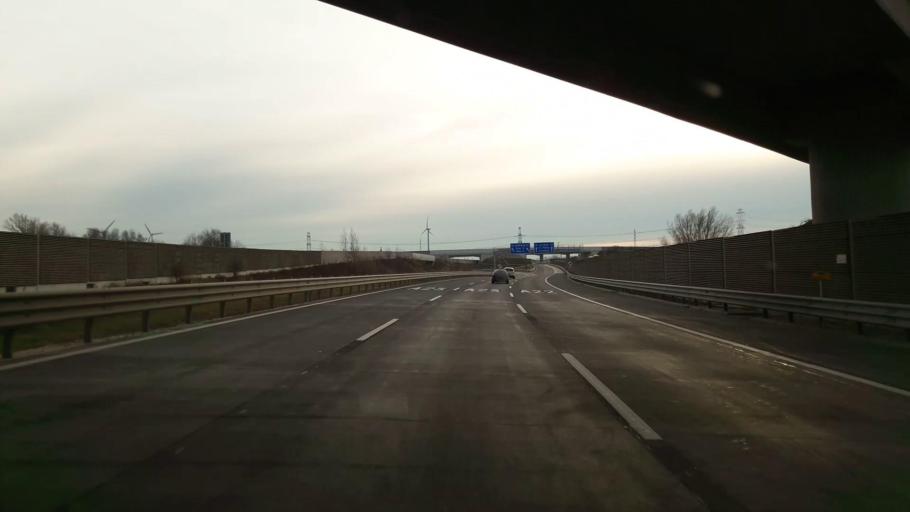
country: AT
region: Lower Austria
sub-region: Politischer Bezirk Mistelbach
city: Grossebersdorf
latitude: 48.3543
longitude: 16.4830
